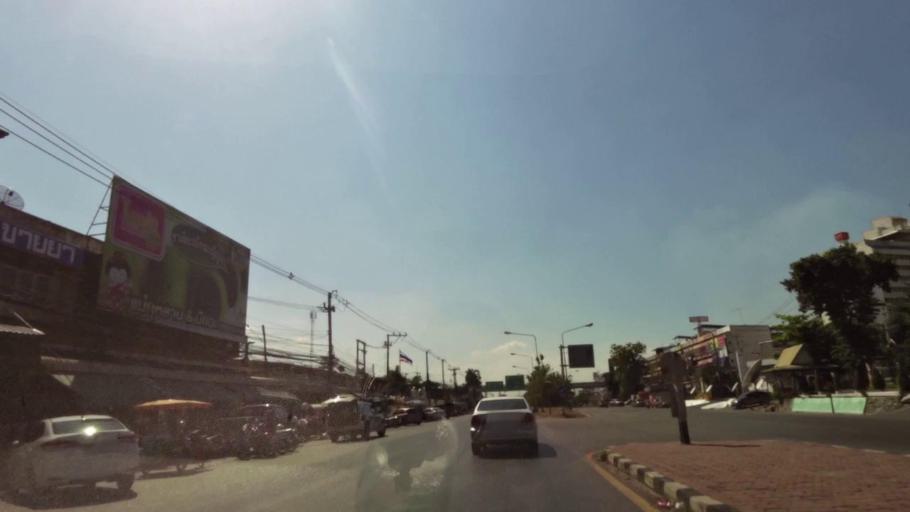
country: TH
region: Nakhon Sawan
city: Nakhon Sawan
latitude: 15.7092
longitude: 100.1157
